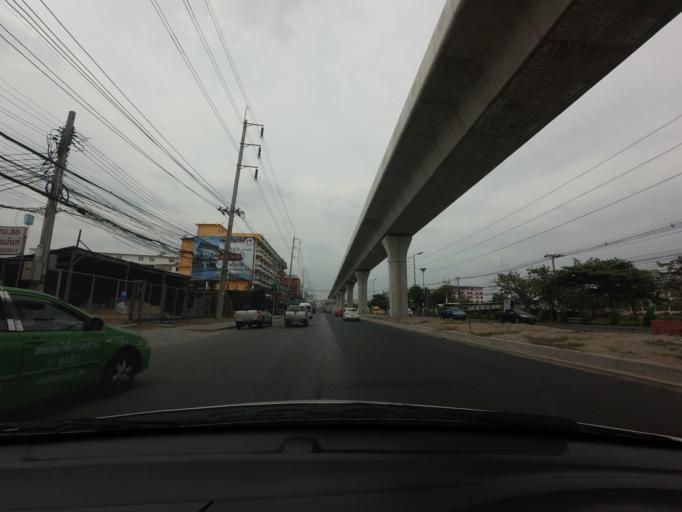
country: TH
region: Samut Prakan
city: Samut Prakan
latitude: 13.5634
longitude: 100.6096
